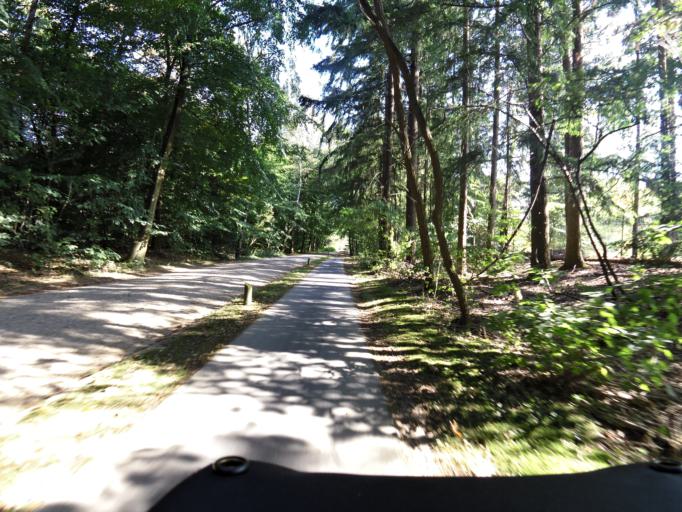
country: NL
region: Gelderland
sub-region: Gemeente Apeldoorn
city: Apeldoorn
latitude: 52.2057
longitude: 5.9160
